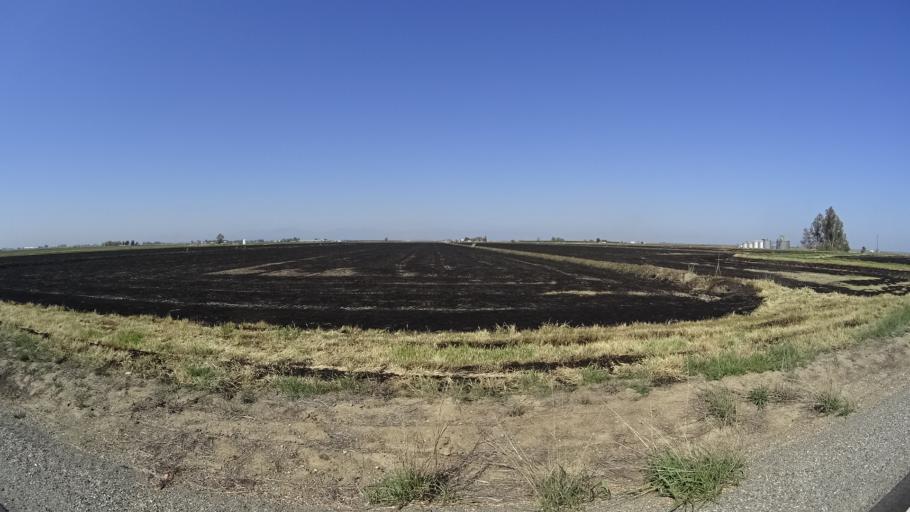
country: US
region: California
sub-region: Glenn County
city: Willows
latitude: 39.5959
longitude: -122.0647
